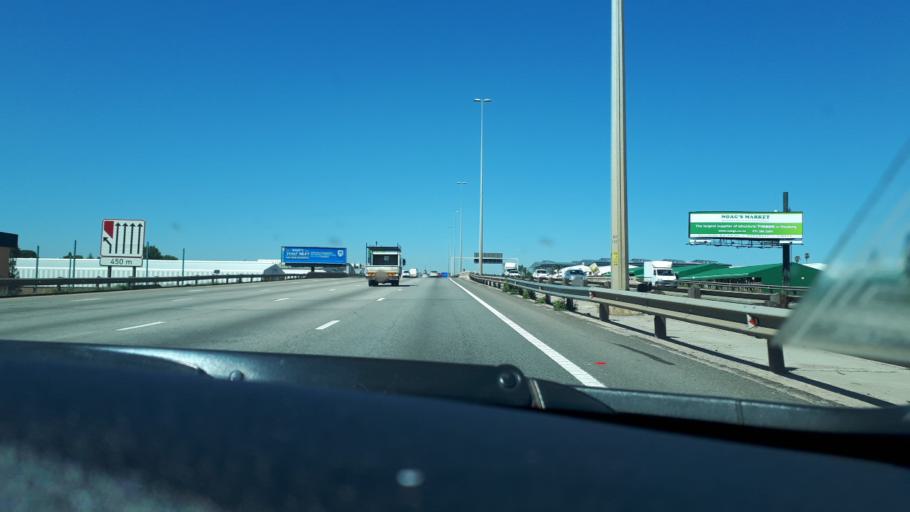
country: ZA
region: Gauteng
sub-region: City of Johannesburg Metropolitan Municipality
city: Modderfontein
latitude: -26.0969
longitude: 28.2624
